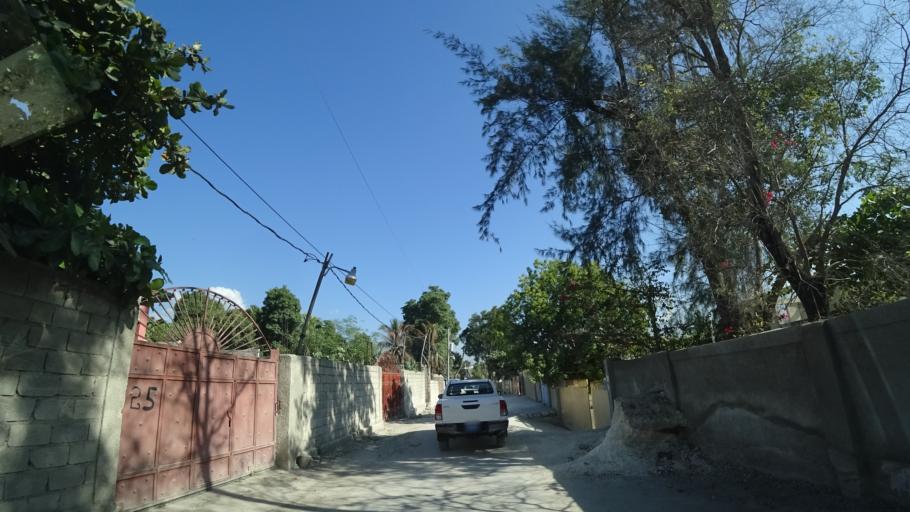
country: HT
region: Ouest
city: Delmas 73
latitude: 18.5574
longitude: -72.2852
